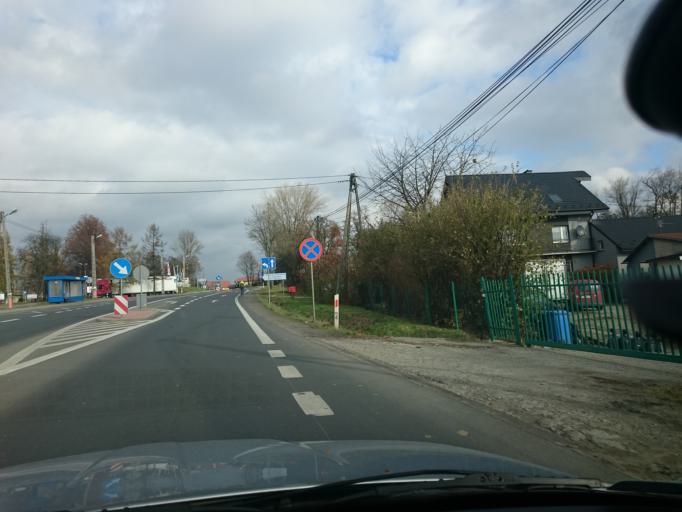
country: PL
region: Lesser Poland Voivodeship
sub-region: Powiat krakowski
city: Zielonki
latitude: 50.1136
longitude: 19.9664
